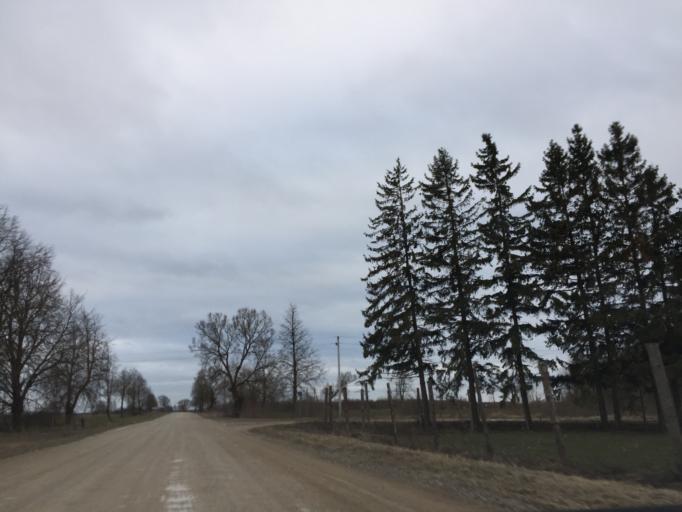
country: LT
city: Zagare
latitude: 56.3505
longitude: 23.2538
